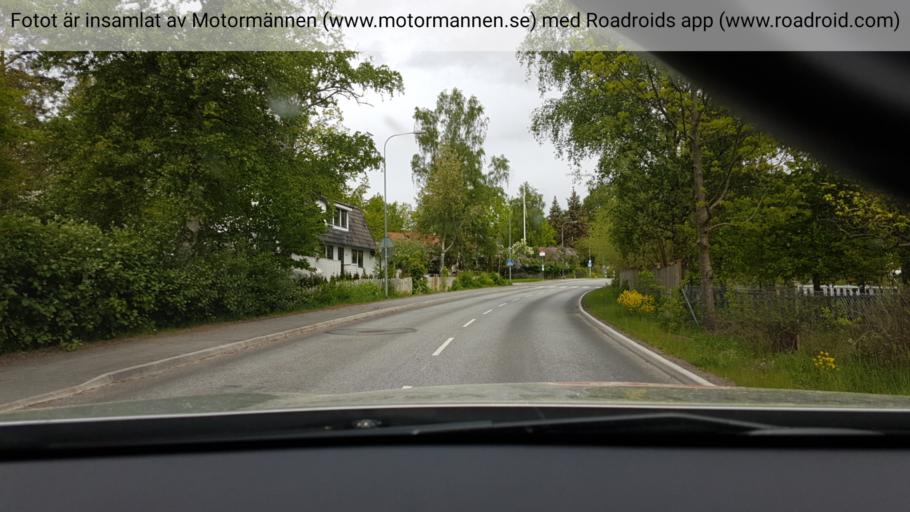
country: SE
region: Stockholm
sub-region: Nacka Kommun
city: Saltsjobaden
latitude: 59.2669
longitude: 18.3059
